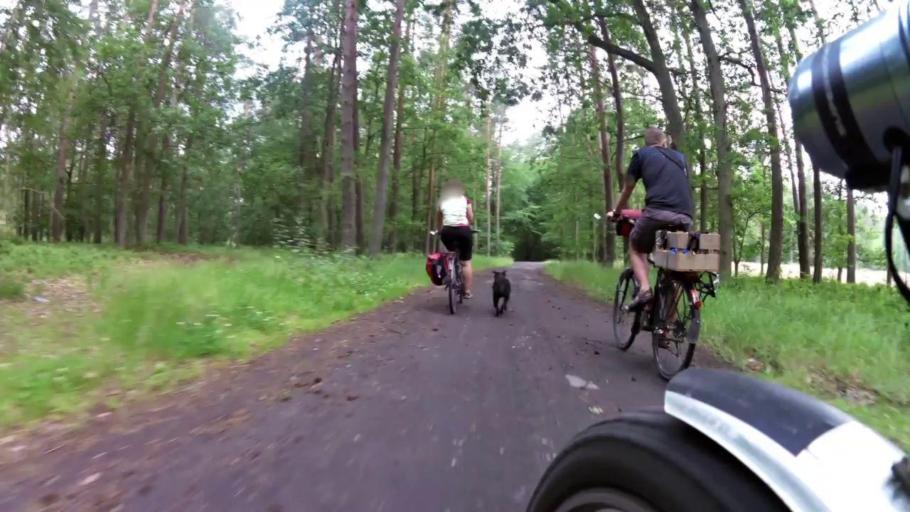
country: PL
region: West Pomeranian Voivodeship
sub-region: Powiat policki
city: Police
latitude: 53.6332
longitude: 14.4708
